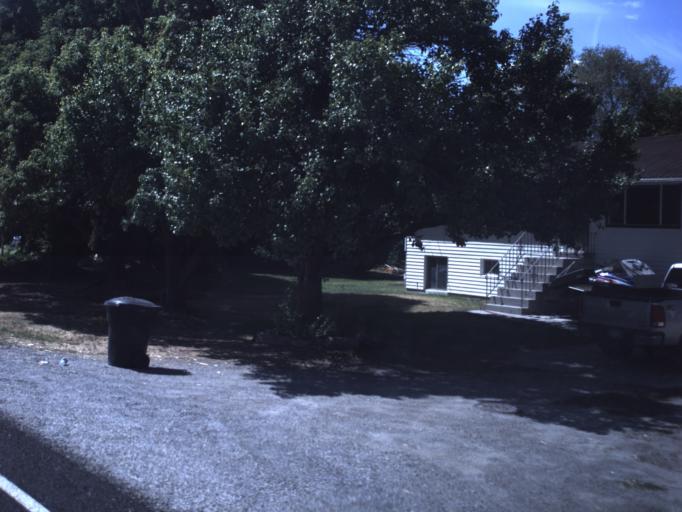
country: US
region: Utah
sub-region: Box Elder County
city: Honeyville
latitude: 41.6218
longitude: -112.1269
